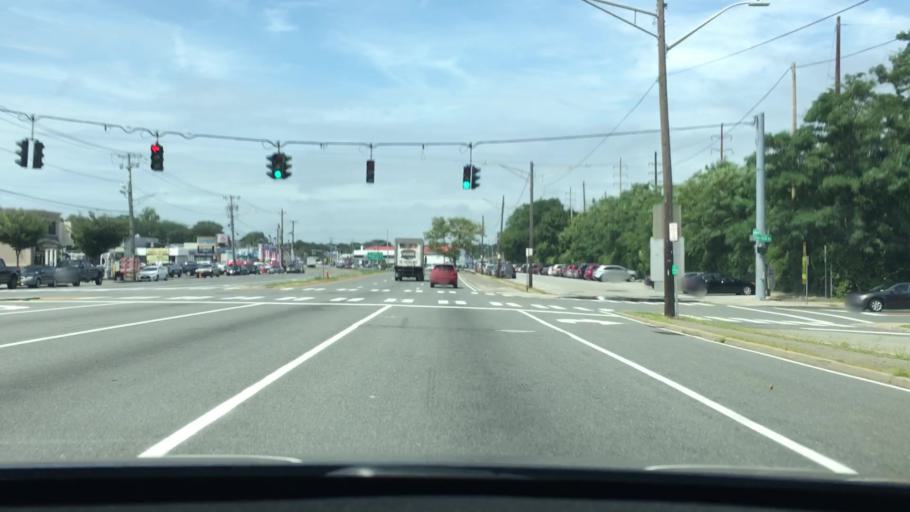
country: US
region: New York
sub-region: Nassau County
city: Wantagh
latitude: 40.6737
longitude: -73.5022
